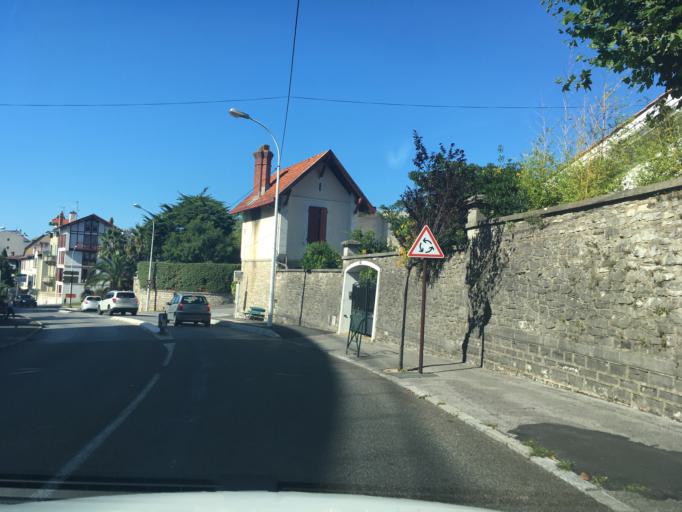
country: FR
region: Aquitaine
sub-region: Departement des Pyrenees-Atlantiques
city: Biarritz
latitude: 43.4770
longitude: -1.5565
